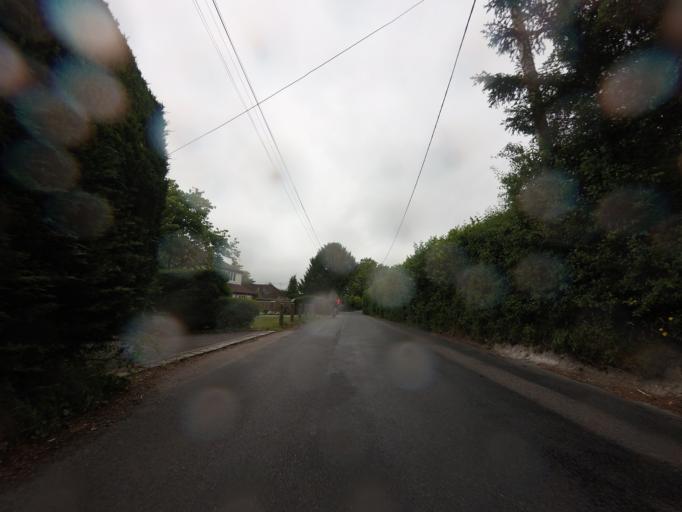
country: GB
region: England
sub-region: Kent
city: Kemsing
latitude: 51.3094
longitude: 0.2201
